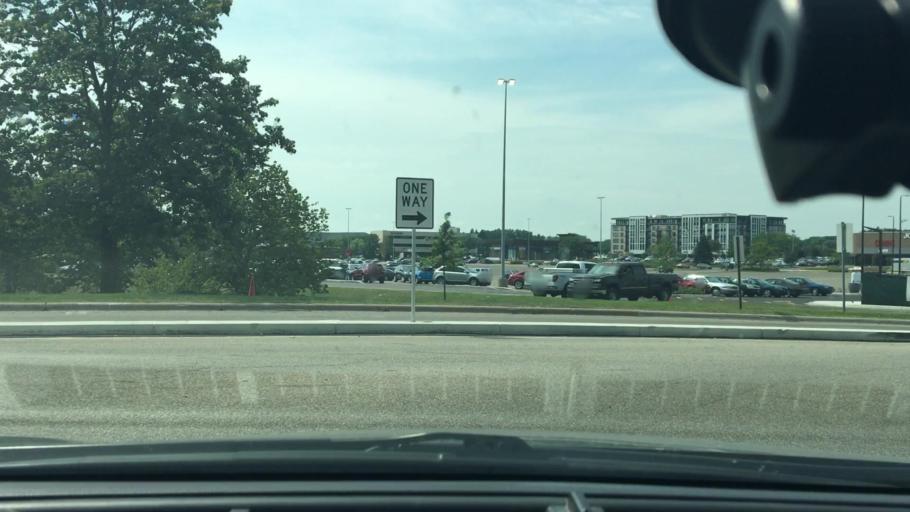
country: US
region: Minnesota
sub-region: Hennepin County
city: Minnetonka Mills
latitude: 44.9702
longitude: -93.4393
